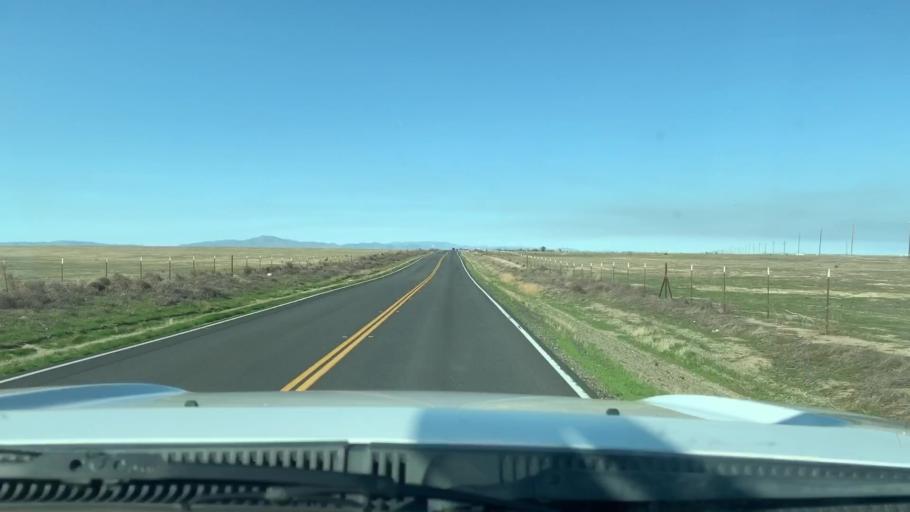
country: US
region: California
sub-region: Kern County
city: Lost Hills
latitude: 35.5917
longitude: -119.8391
